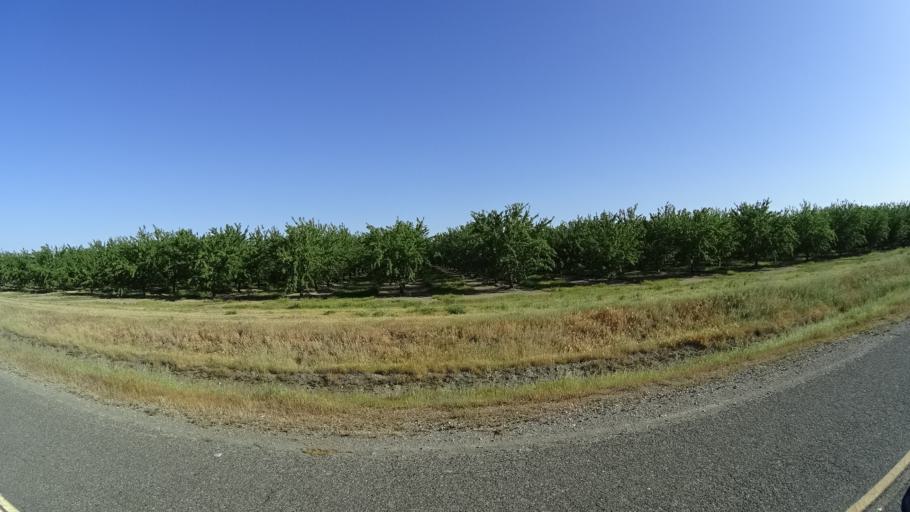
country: US
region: California
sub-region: Glenn County
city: Orland
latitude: 39.6961
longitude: -122.1208
